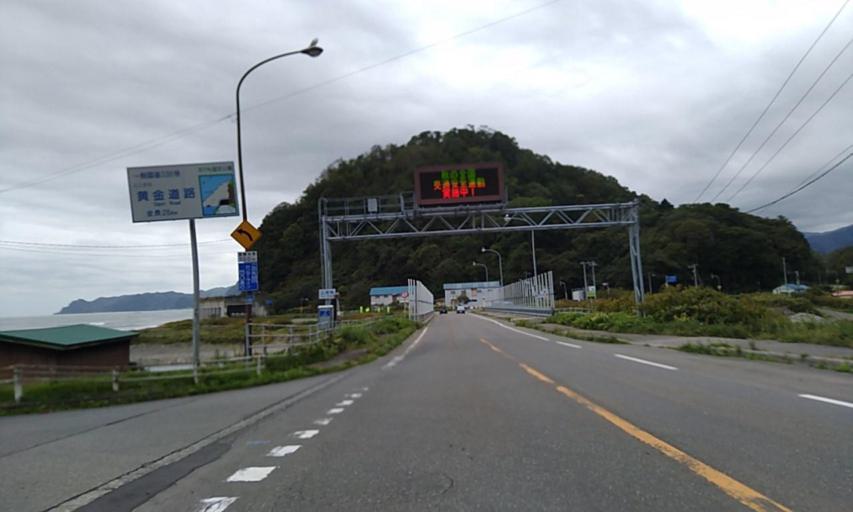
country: JP
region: Hokkaido
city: Obihiro
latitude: 42.2818
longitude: 143.3181
